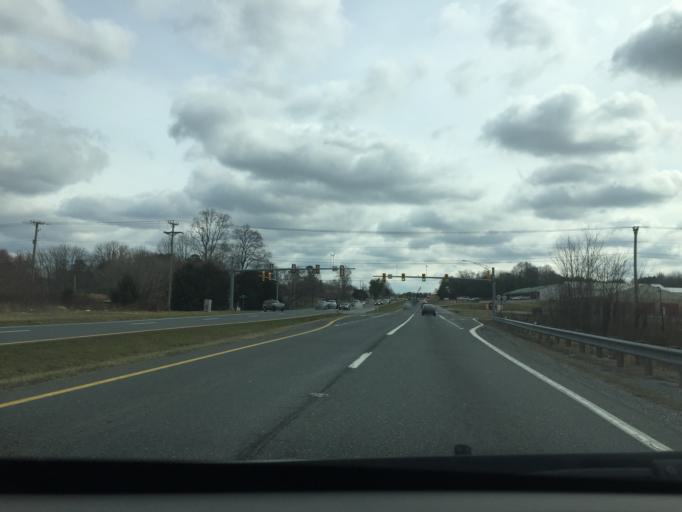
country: US
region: Virginia
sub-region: Campbell County
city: Timberlake
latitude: 37.3052
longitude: -79.2820
